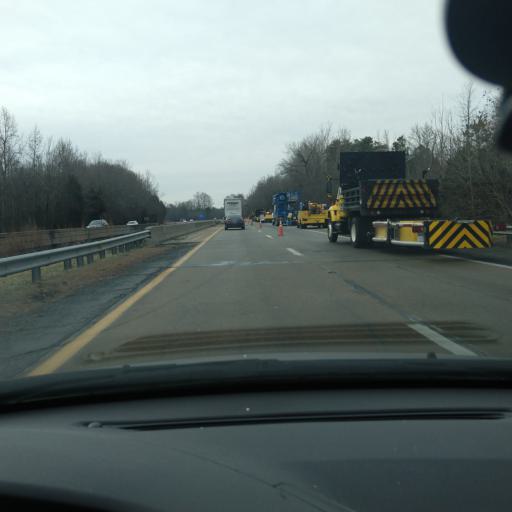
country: US
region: North Carolina
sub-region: Forsyth County
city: Winston-Salem
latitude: 36.0259
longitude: -80.2369
